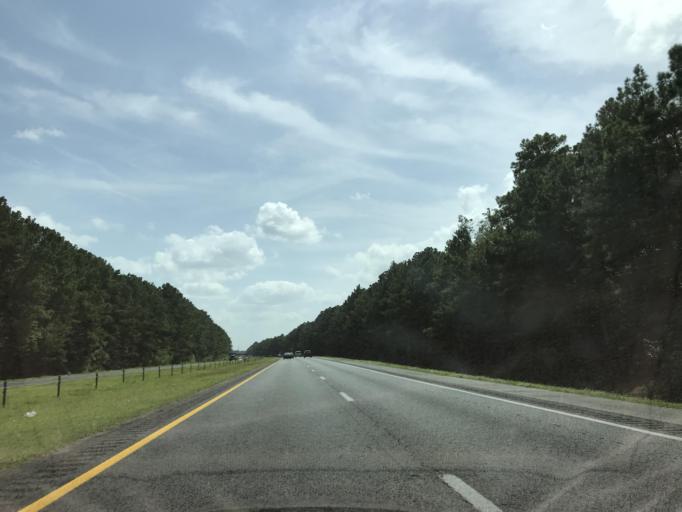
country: US
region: North Carolina
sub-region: Duplin County
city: Wallace
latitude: 34.7107
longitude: -77.9457
